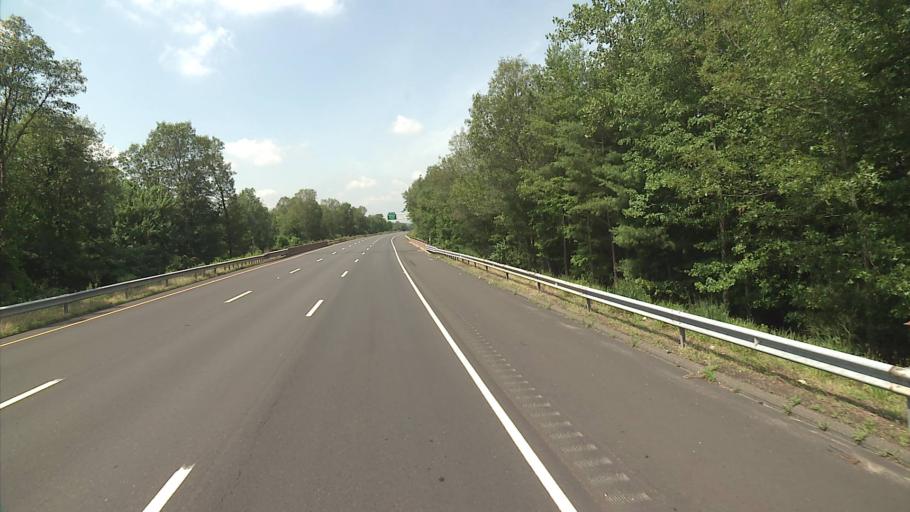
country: US
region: Connecticut
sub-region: Hartford County
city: Manchester
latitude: 41.7710
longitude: -72.4726
